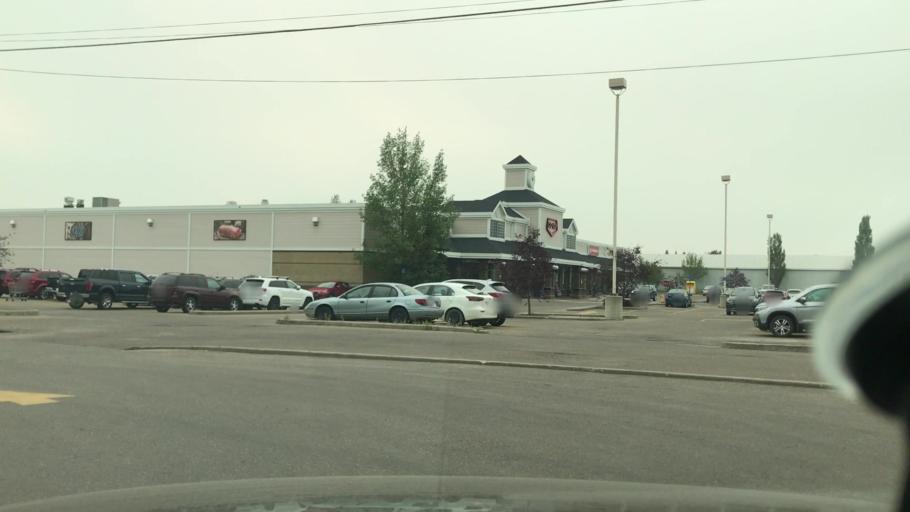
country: CA
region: Alberta
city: Leduc
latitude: 53.2705
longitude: -113.5511
